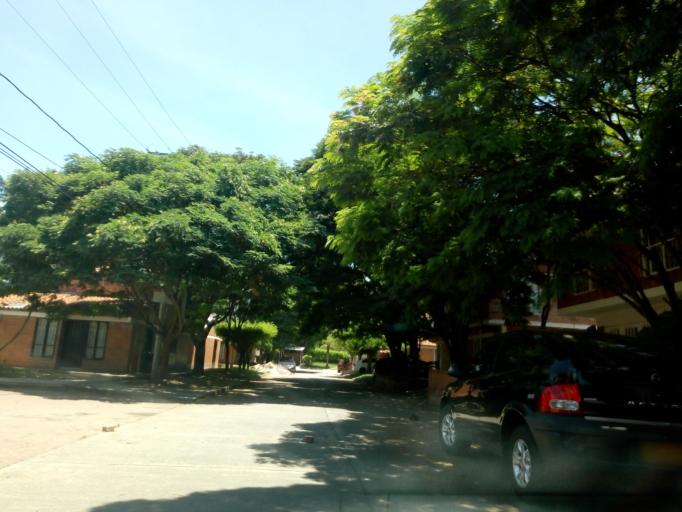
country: CO
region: Valle del Cauca
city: Cartago
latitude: 4.7350
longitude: -75.9111
